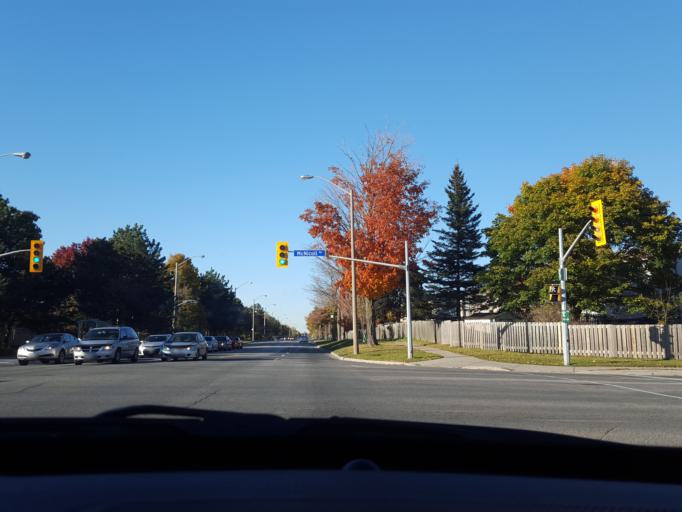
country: CA
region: Ontario
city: Scarborough
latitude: 43.8155
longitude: -79.2817
